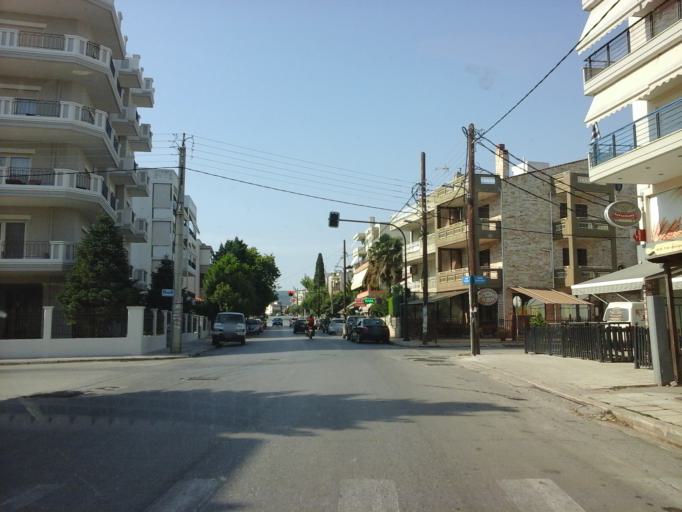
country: GR
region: East Macedonia and Thrace
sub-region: Nomos Evrou
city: Alexandroupoli
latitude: 40.8589
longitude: 25.8696
